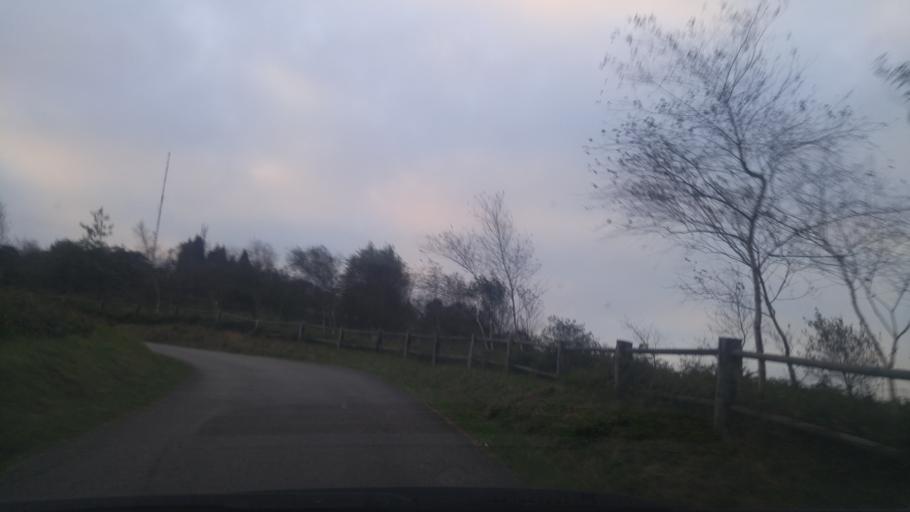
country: ES
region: Asturias
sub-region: Province of Asturias
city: Oviedo
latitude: 43.3846
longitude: -5.8603
